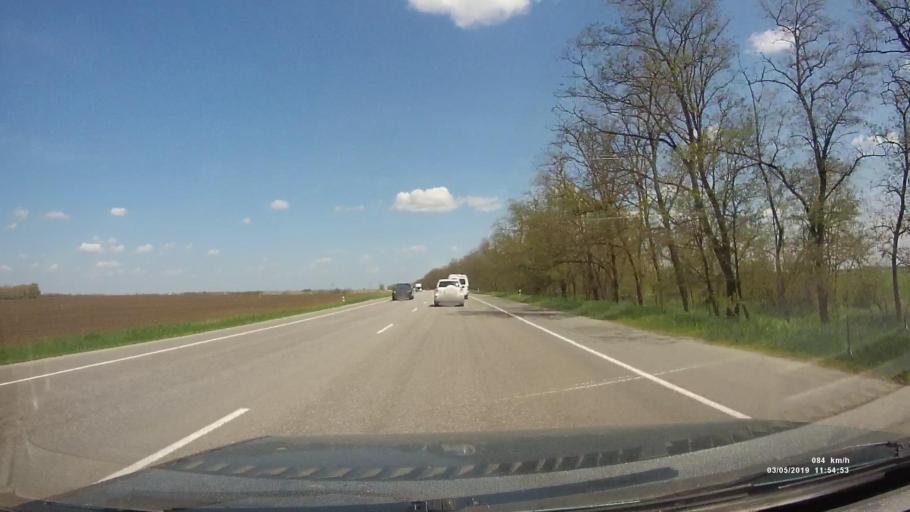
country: RU
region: Rostov
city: Bagayevskaya
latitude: 47.1744
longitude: 40.2860
